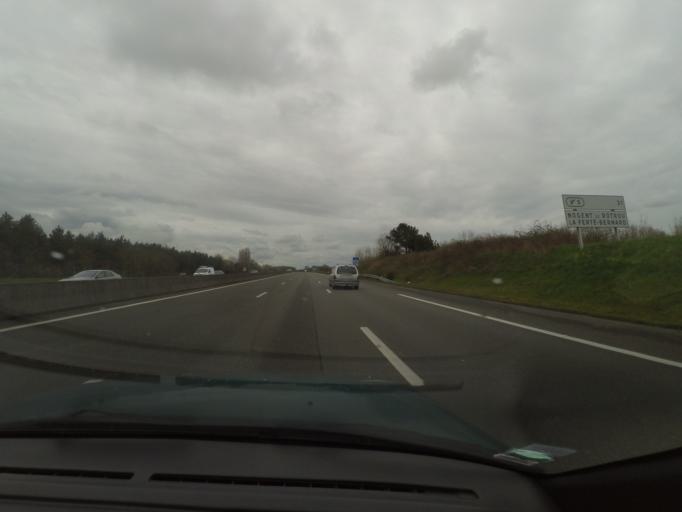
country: FR
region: Pays de la Loire
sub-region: Departement de la Sarthe
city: Champagne
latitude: 48.0509
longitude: 0.3084
